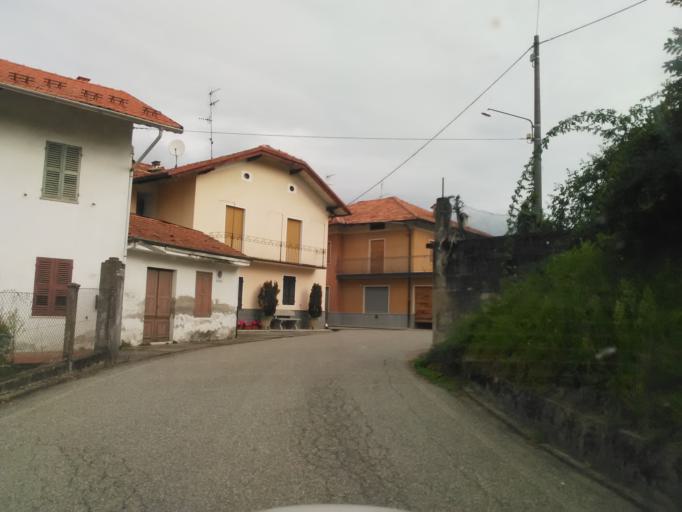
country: IT
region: Piedmont
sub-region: Provincia di Biella
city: Frazione Chiesa
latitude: 45.6925
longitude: 8.2135
